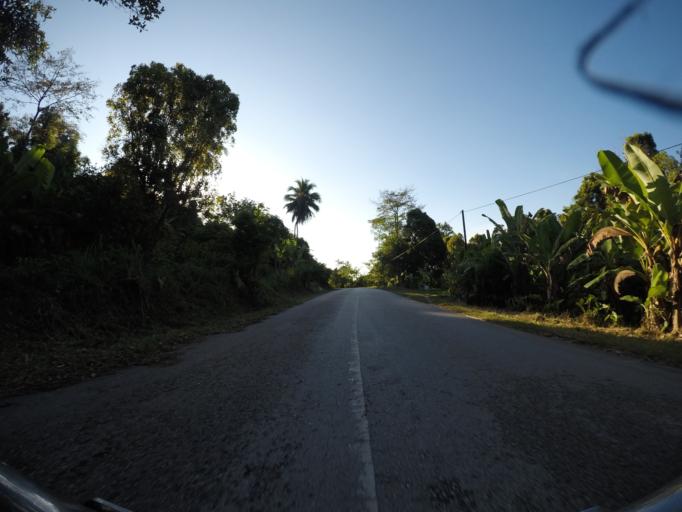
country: TZ
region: Pemba South
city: Mtambile
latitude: -5.3777
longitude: 39.6900
